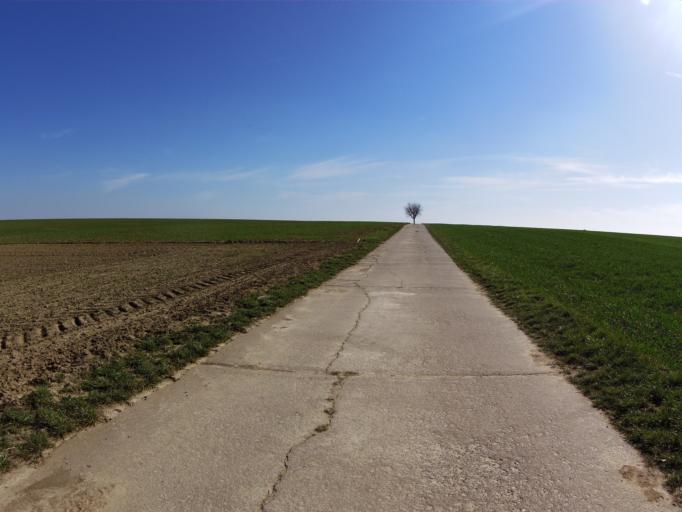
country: DE
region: Bavaria
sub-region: Regierungsbezirk Unterfranken
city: Prosselsheim
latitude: 49.8528
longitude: 10.1211
